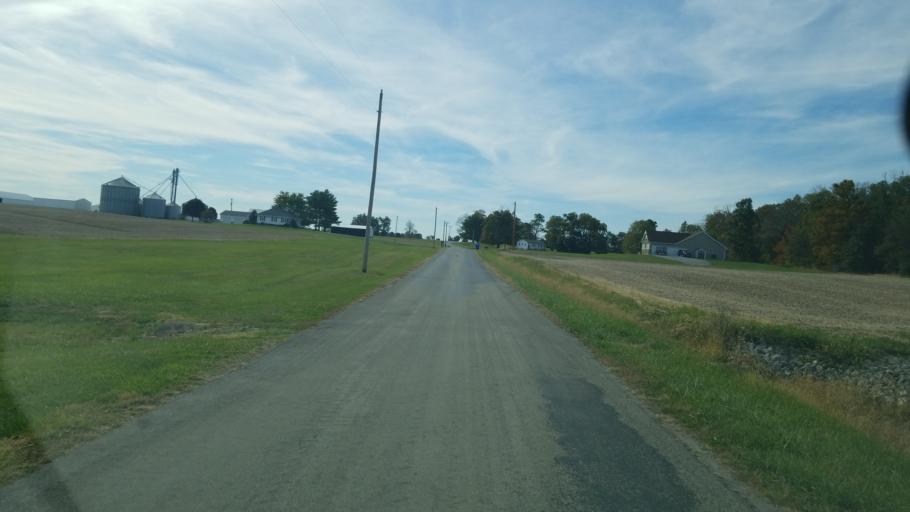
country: US
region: Ohio
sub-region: Highland County
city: Leesburg
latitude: 39.3299
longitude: -83.5591
